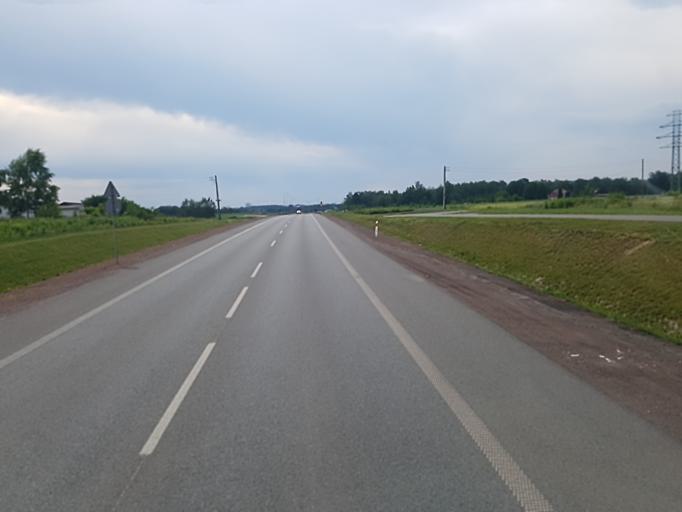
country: PL
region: Silesian Voivodeship
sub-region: Jastrzebie-Zdroj
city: Jastrzebie Zdroj
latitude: 49.9711
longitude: 18.6104
